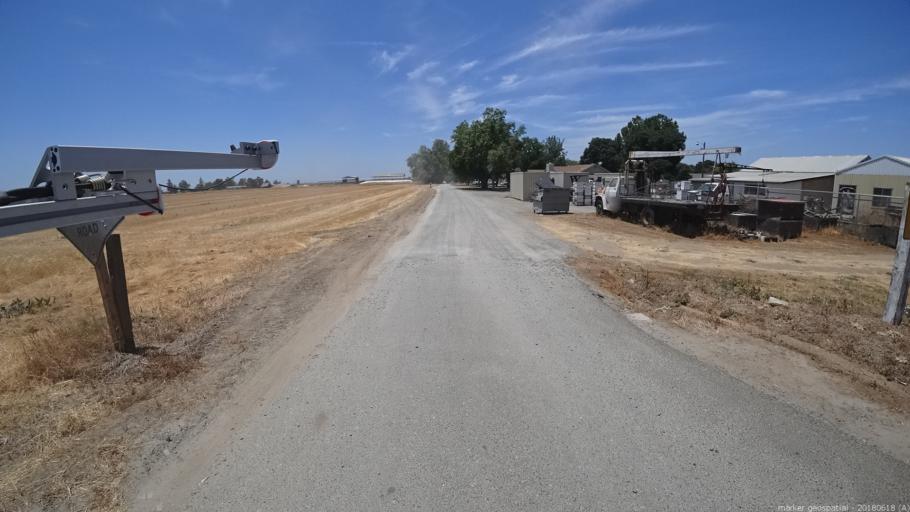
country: US
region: California
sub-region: Madera County
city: Parkwood
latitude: 36.9129
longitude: -120.0925
